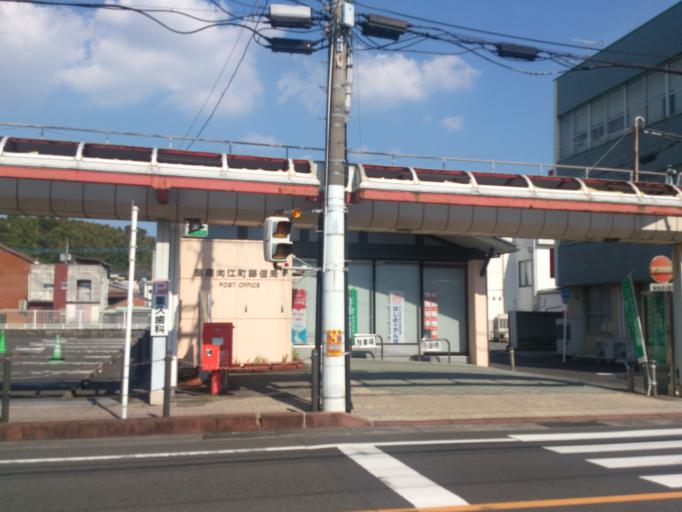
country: JP
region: Kagoshima
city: Kanoya
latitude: 31.3843
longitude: 130.8516
